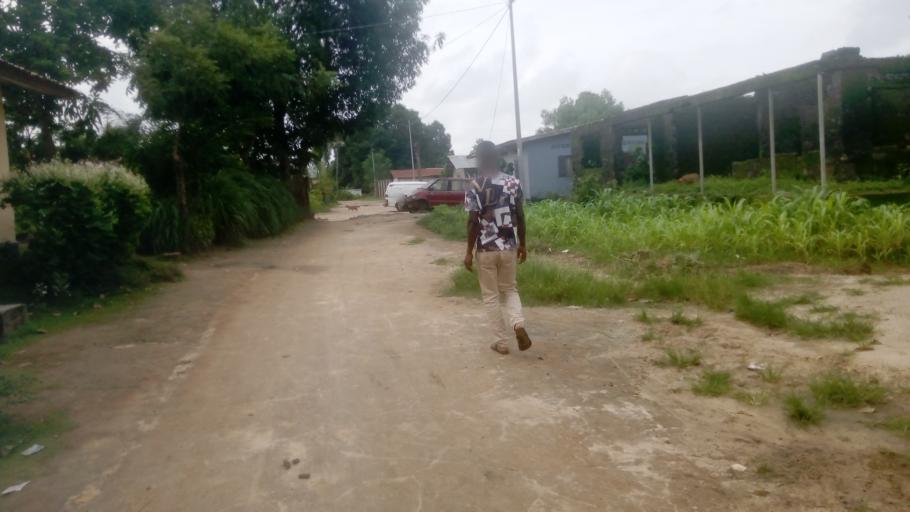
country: SL
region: Northern Province
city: Lunsar
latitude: 8.6881
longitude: -12.5383
